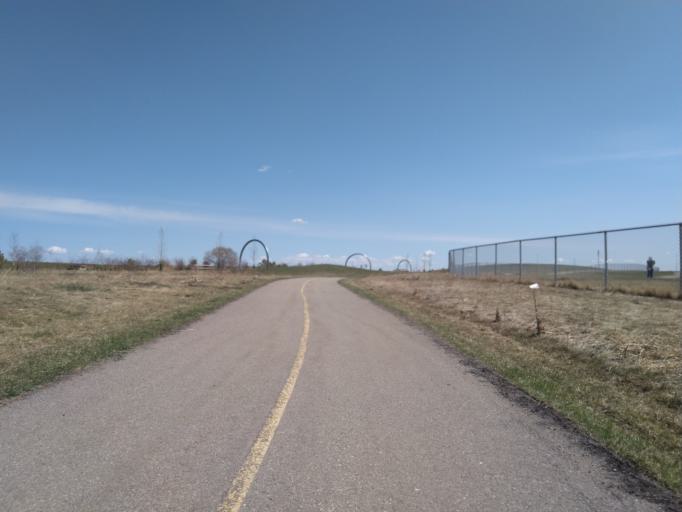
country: CA
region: Alberta
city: Chestermere
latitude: 51.1109
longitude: -113.9278
